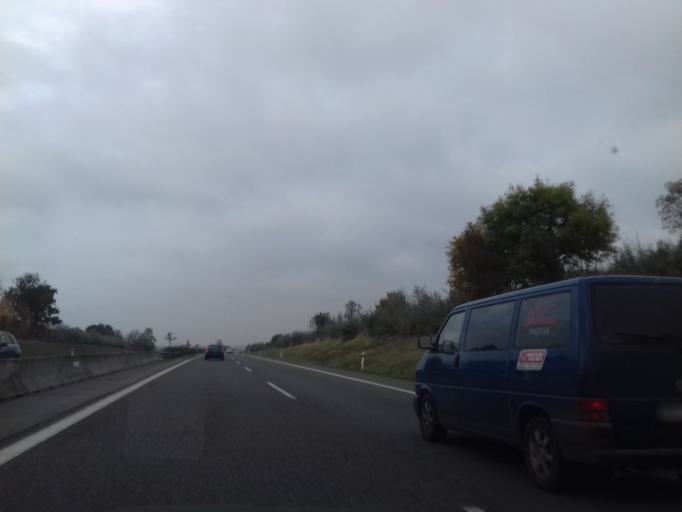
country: SK
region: Bratislavsky
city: Stupava
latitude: 48.2745
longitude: 17.0089
